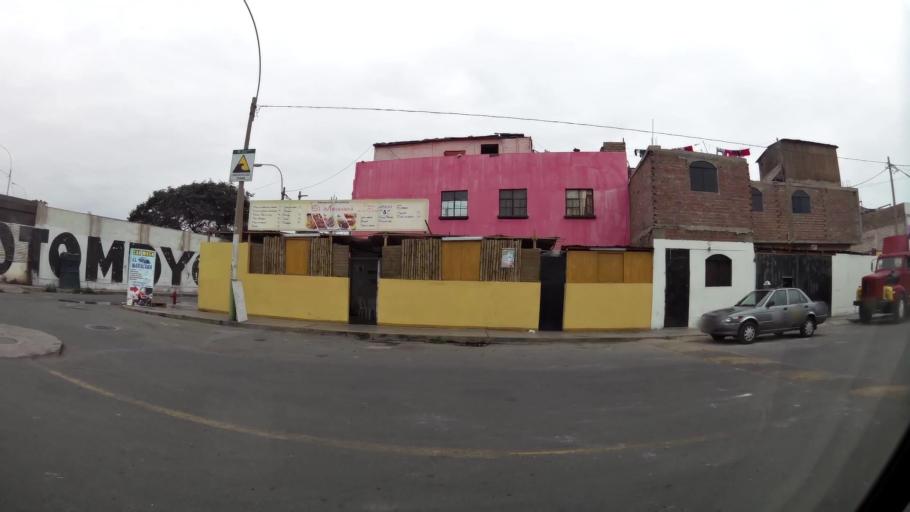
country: PE
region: Callao
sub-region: Callao
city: Callao
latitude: -12.0484
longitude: -77.1367
